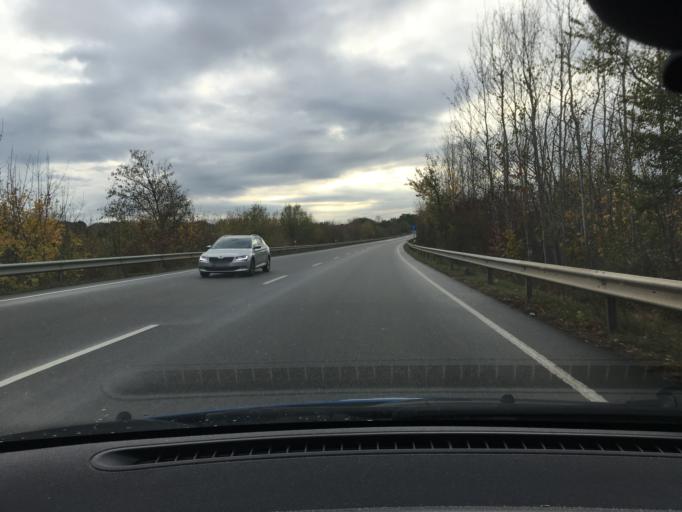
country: DE
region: Schleswig-Holstein
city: Alt Molln
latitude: 53.6195
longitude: 10.6612
